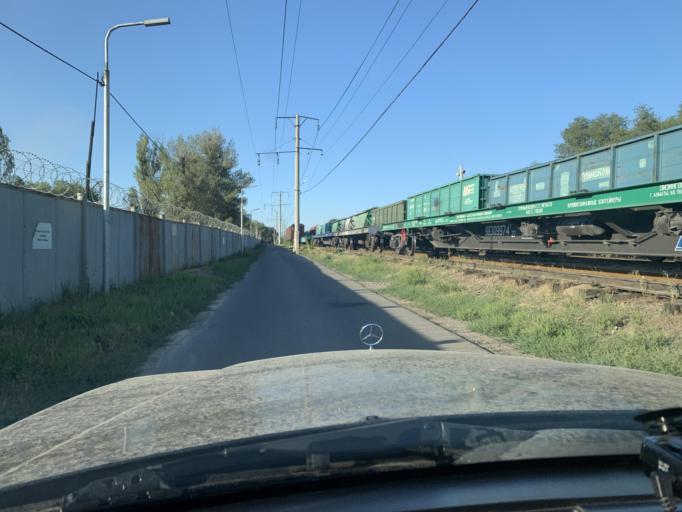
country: KZ
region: Almaty Oblysy
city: Energeticheskiy
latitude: 43.3865
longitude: 76.9981
